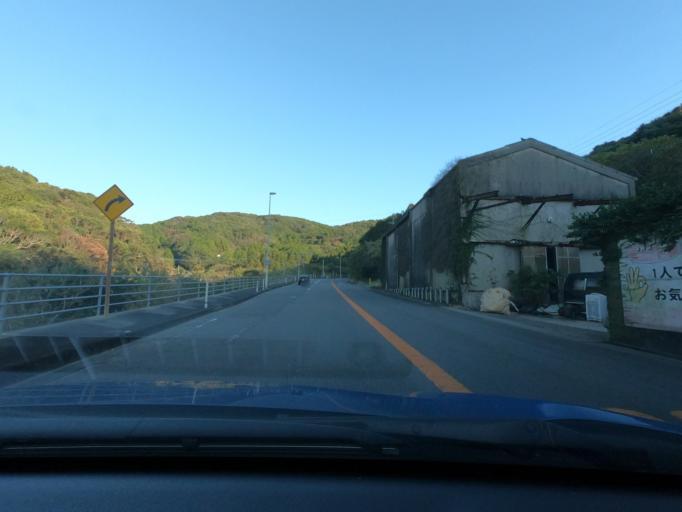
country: JP
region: Kagoshima
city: Akune
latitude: 31.9306
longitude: 130.2220
